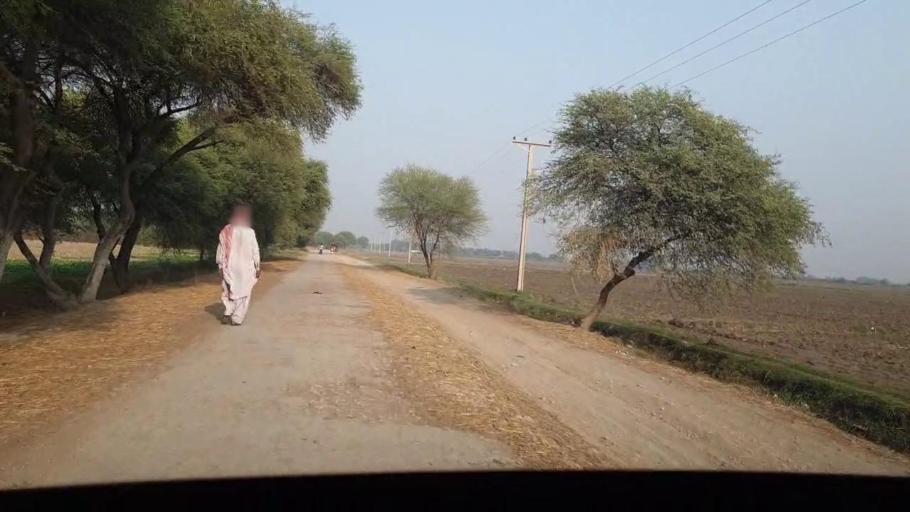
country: PK
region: Sindh
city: Chuhar Jamali
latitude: 24.2499
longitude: 68.0963
